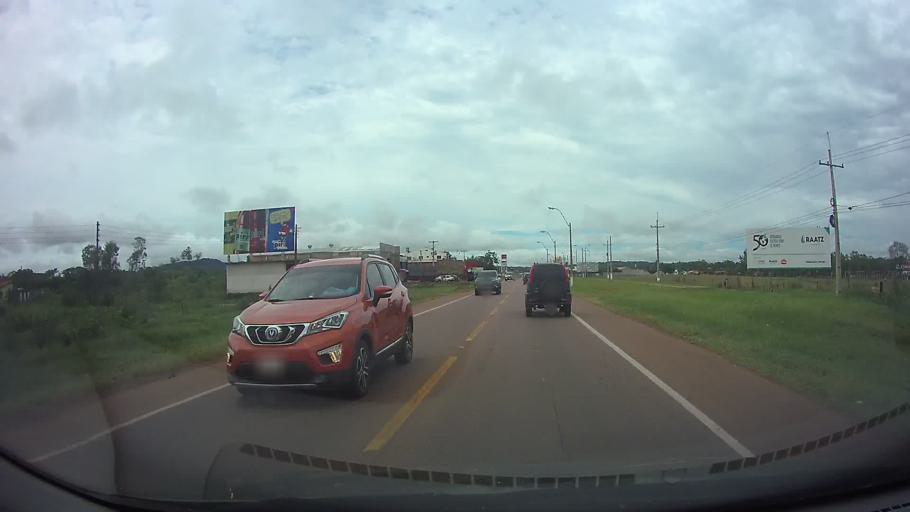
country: PY
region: Paraguari
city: Carapegua
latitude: -25.7606
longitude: -57.2319
